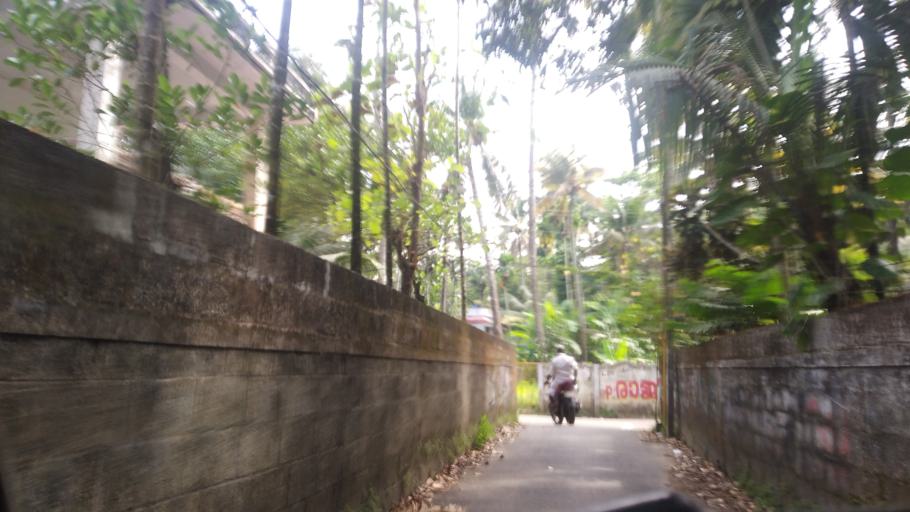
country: IN
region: Kerala
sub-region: Ernakulam
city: Elur
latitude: 10.0861
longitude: 76.2060
